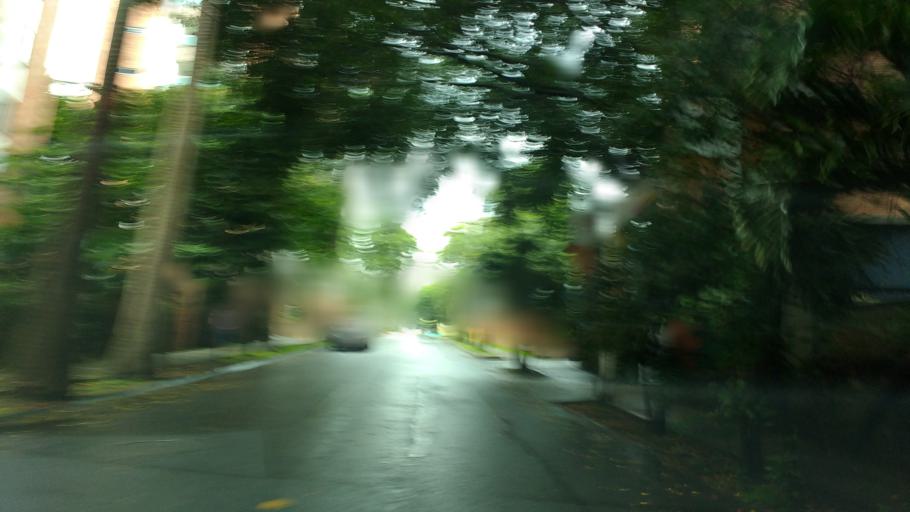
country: CO
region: Antioquia
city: Envigado
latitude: 6.1865
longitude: -75.5793
